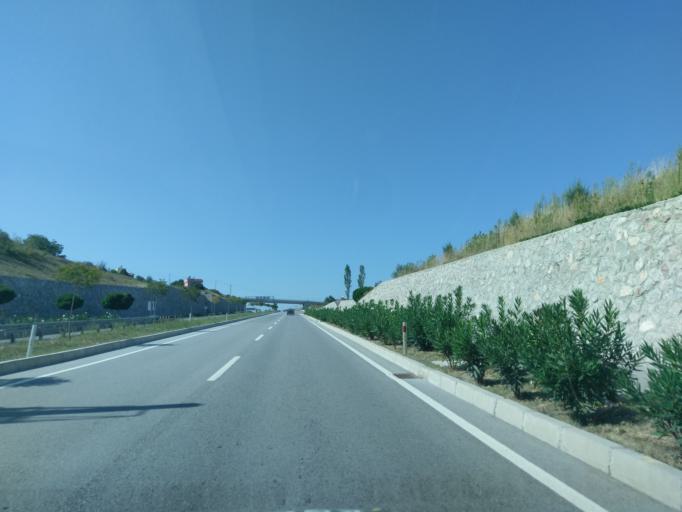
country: TR
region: Sinop
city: Gerze
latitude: 41.7924
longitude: 35.1883
